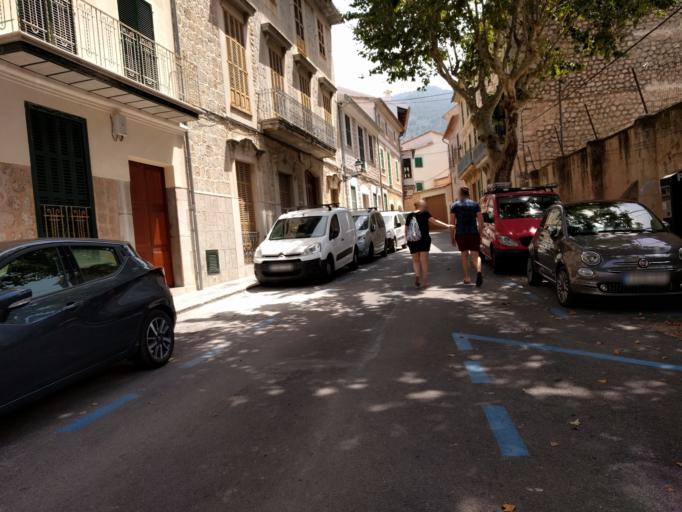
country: ES
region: Balearic Islands
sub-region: Illes Balears
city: Soller
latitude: 39.7683
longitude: 2.7156
